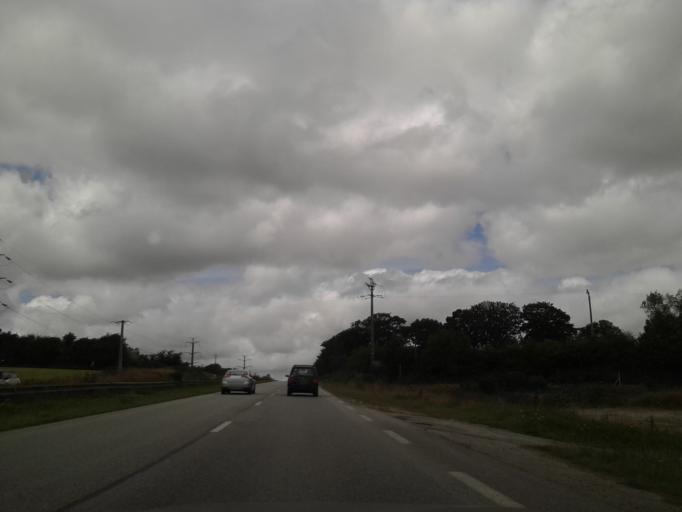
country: FR
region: Lower Normandy
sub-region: Departement de la Manche
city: La Glacerie
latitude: 49.5808
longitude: -1.5867
